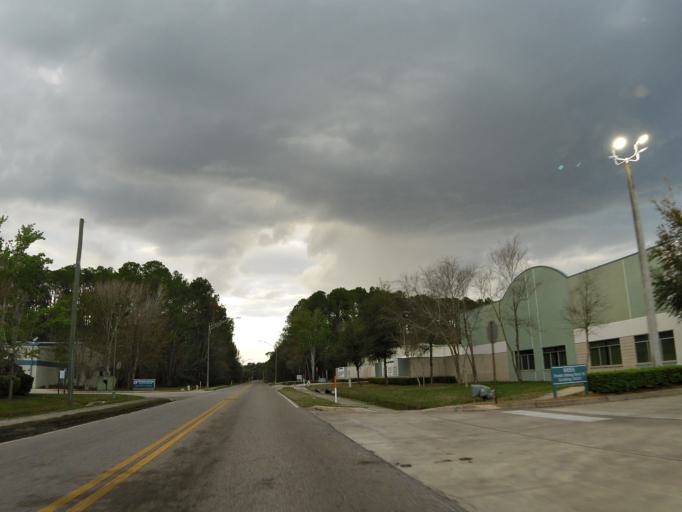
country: US
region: Florida
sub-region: Saint Johns County
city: Fruit Cove
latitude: 30.1887
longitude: -81.5746
